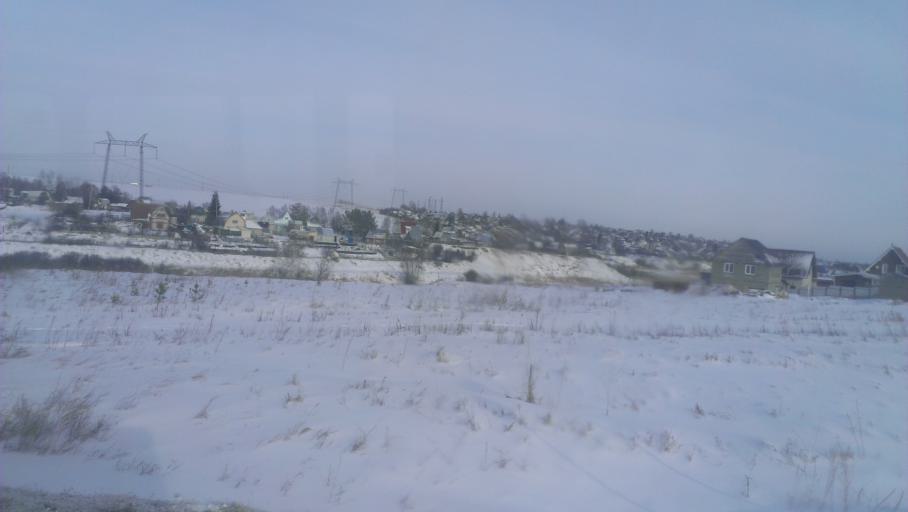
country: RU
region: Altai Krai
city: Gon'ba
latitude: 53.4141
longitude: 83.5515
